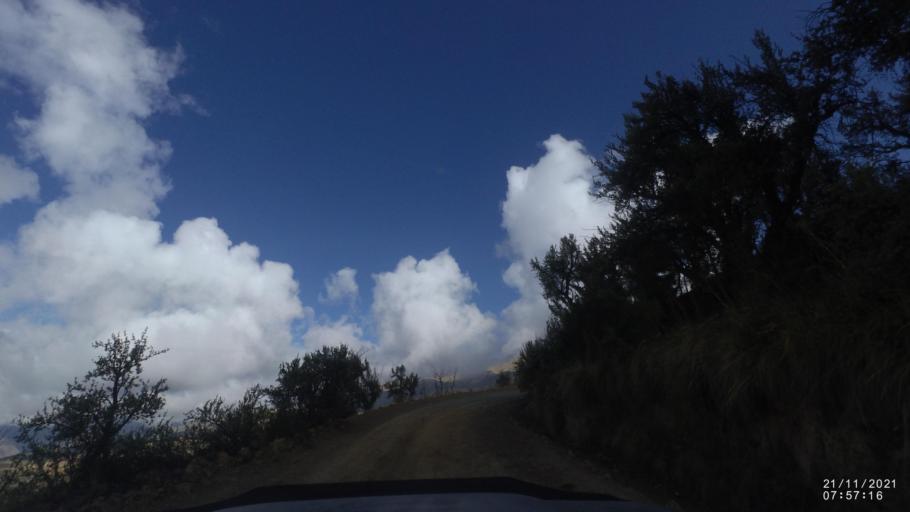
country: BO
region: Cochabamba
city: Cochabamba
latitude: -17.2964
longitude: -66.2205
